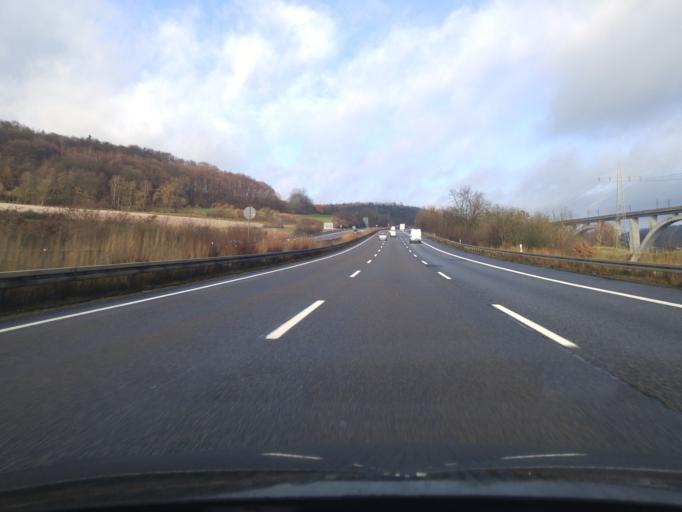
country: DE
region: Hesse
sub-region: Regierungsbezirk Kassel
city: Kirchheim
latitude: 50.8501
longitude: 9.5858
